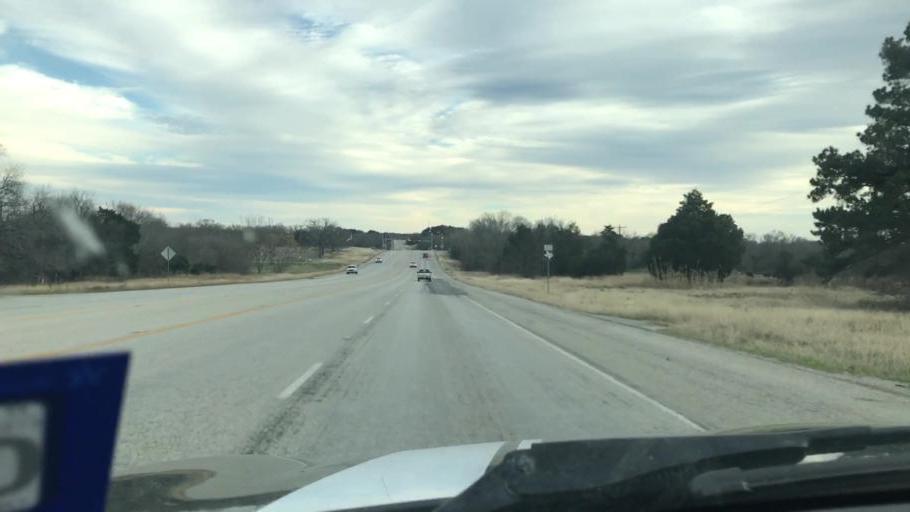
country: US
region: Texas
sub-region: Bastrop County
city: Camp Swift
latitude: 30.2831
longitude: -97.2449
